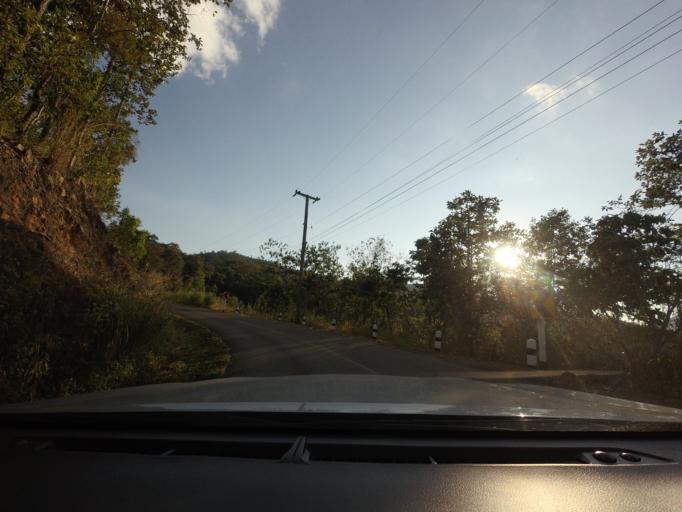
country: TH
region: Chiang Mai
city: Phrao
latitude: 19.4881
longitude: 99.1664
